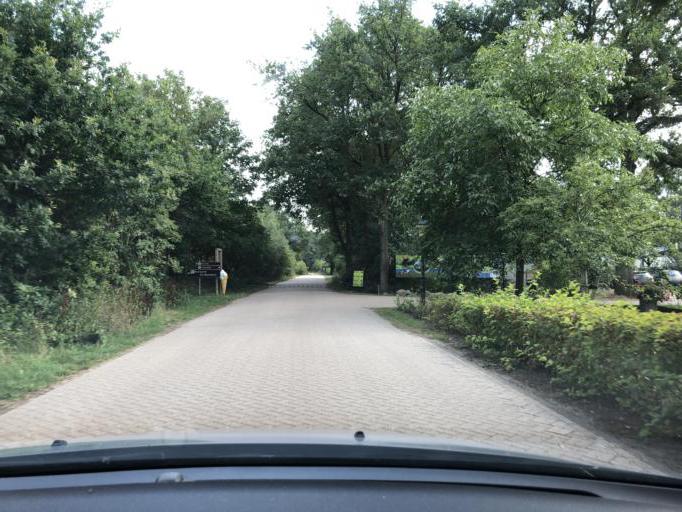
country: NL
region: Overijssel
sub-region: Gemeente Dalfsen
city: Dalfsen
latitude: 52.6112
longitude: 6.3714
